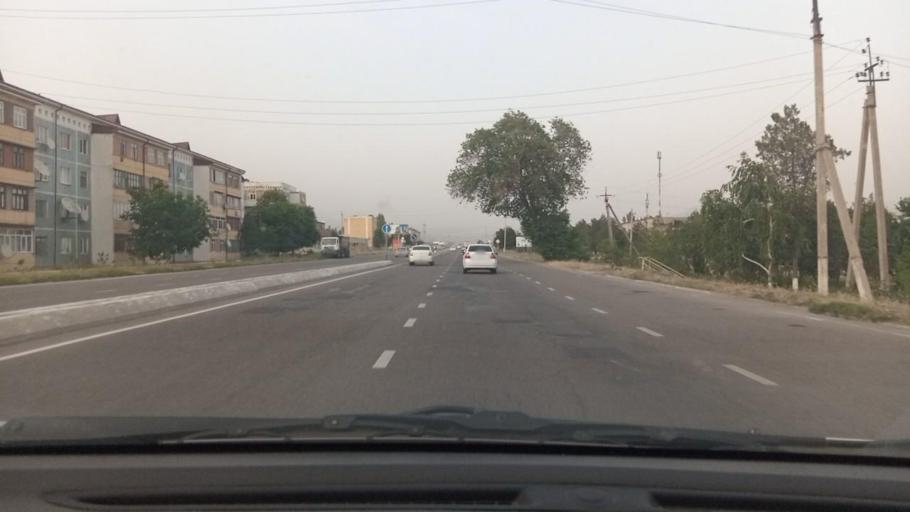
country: UZ
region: Toshkent
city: Angren
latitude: 41.0114
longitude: 70.1006
